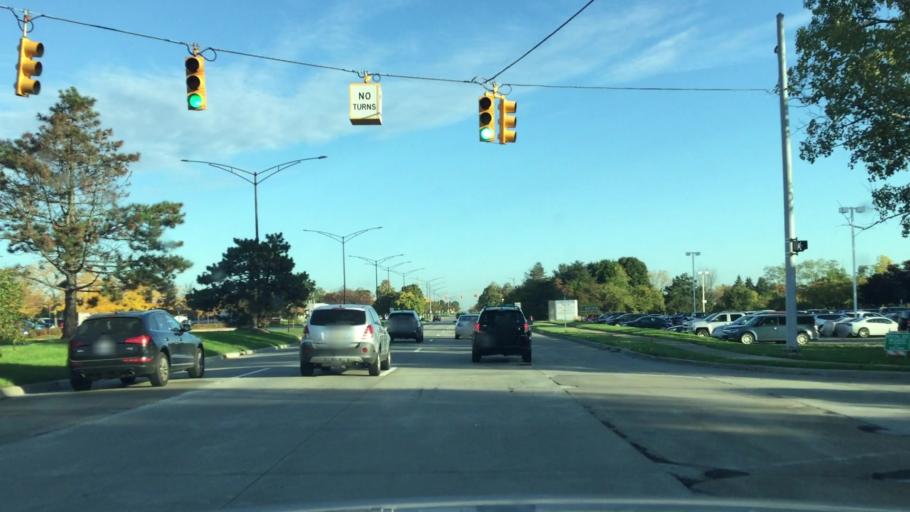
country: US
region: Michigan
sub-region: Oakland County
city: Troy
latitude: 42.5961
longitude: -83.1687
